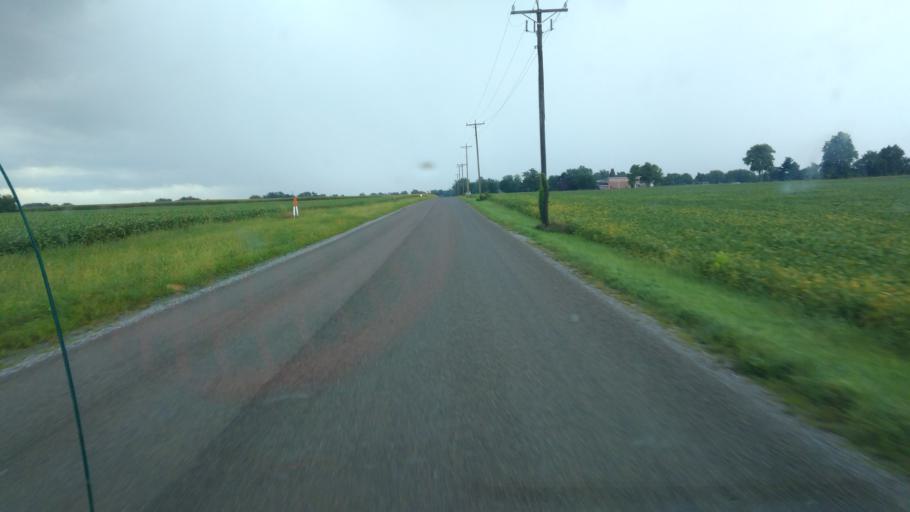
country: US
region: Ohio
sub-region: Hardin County
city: Kenton
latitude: 40.6547
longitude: -83.5761
